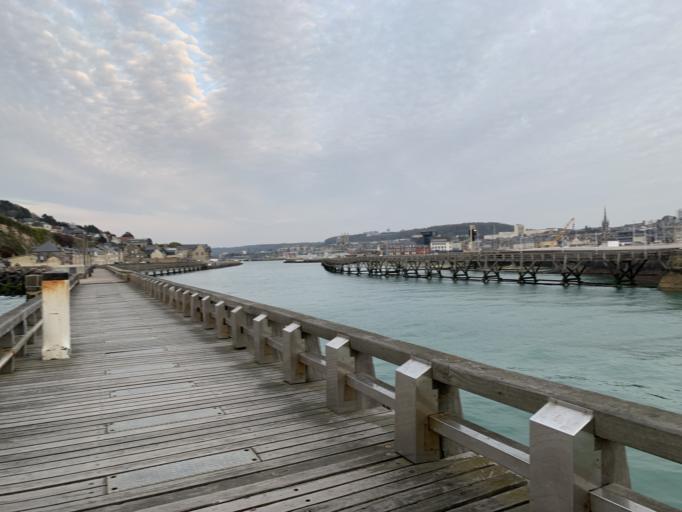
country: FR
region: Haute-Normandie
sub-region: Departement de la Seine-Maritime
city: Fecamp
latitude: 49.7656
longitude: 0.3634
